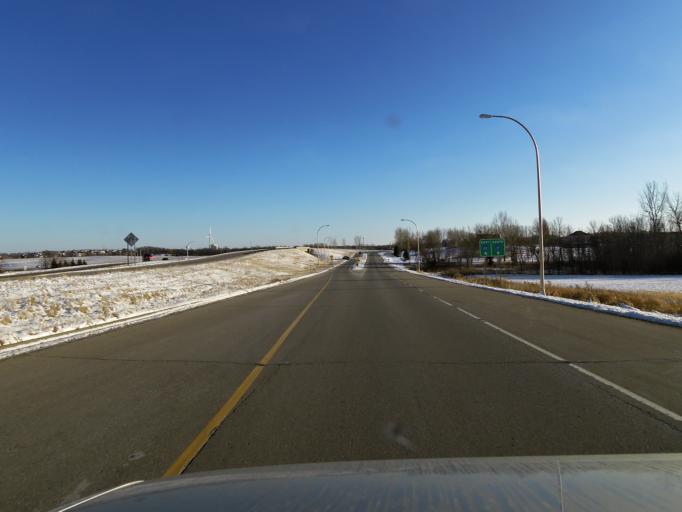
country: US
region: Minnesota
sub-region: Scott County
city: Shakopee
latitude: 44.7483
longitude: -93.5031
